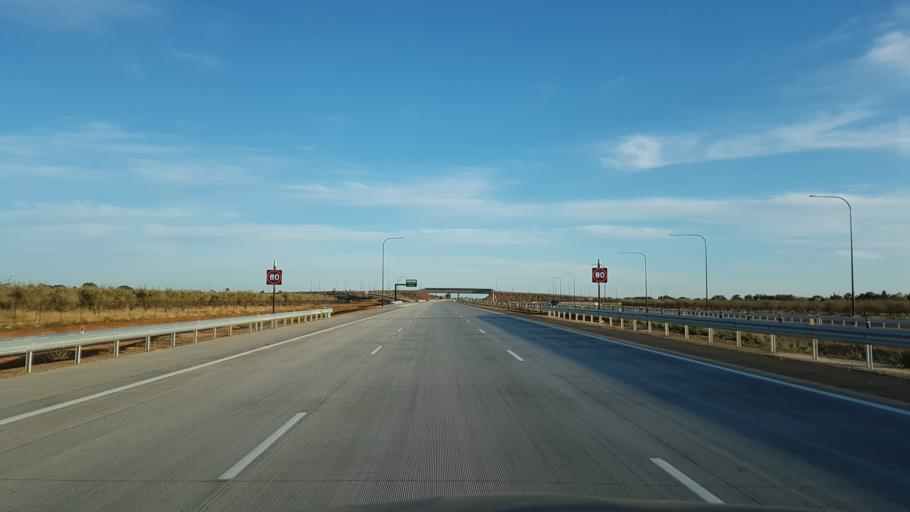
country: AU
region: South Australia
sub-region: Salisbury
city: Salisbury
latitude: -34.7385
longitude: 138.5785
